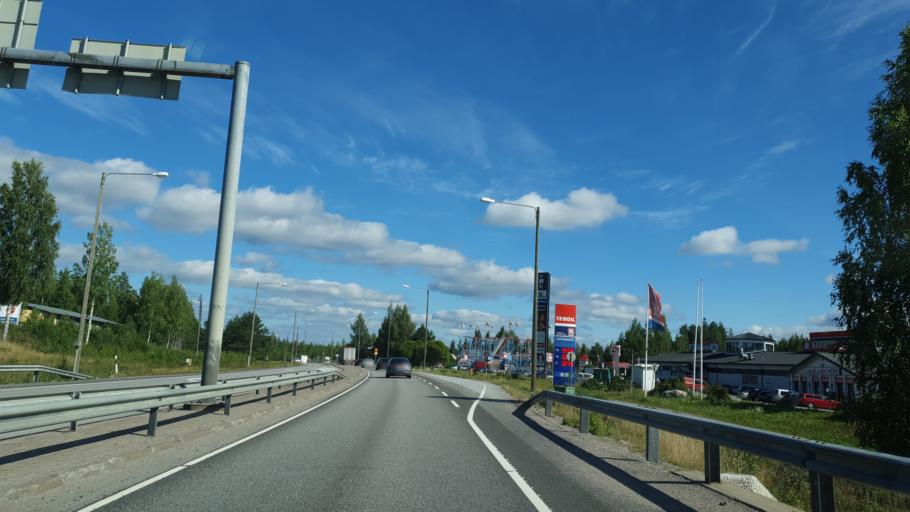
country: FI
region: Central Finland
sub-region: Jyvaeskylae
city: Toivakka
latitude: 62.2469
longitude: 26.1348
